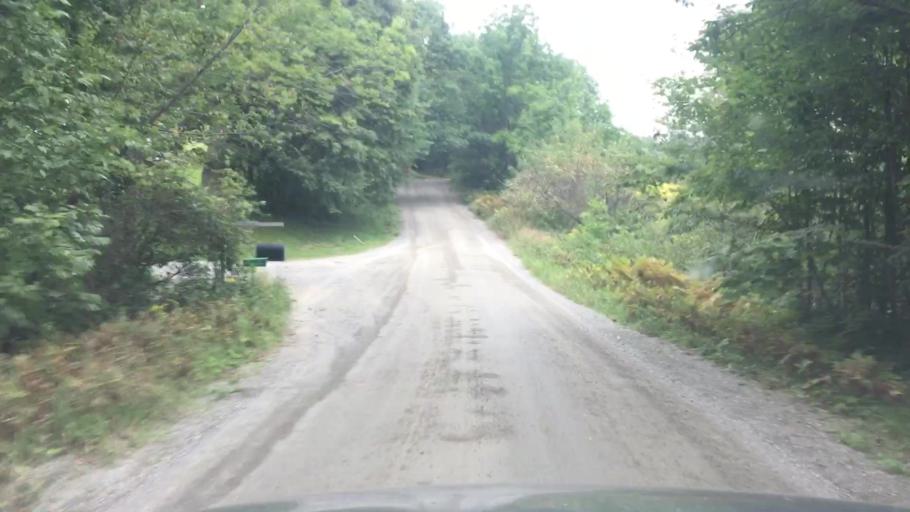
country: US
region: Vermont
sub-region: Windham County
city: Dover
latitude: 42.8599
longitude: -72.7811
